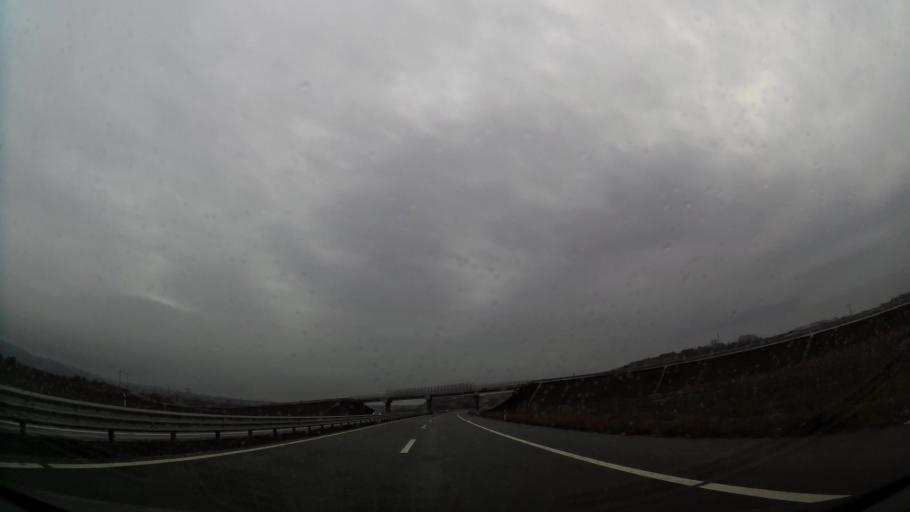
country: XK
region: Ferizaj
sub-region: Komuna e Ferizajt
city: Ferizaj
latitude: 42.4433
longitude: 21.1971
